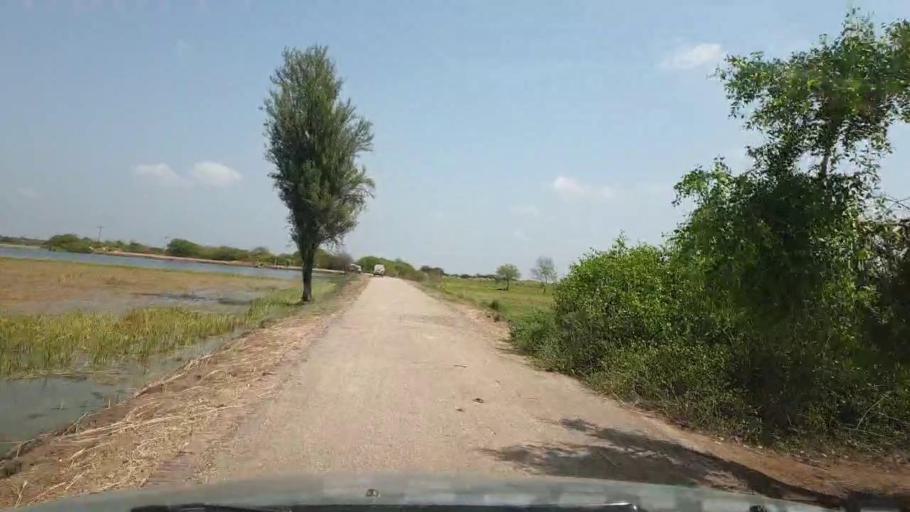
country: PK
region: Sindh
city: Rajo Khanani
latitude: 25.0267
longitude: 68.9225
